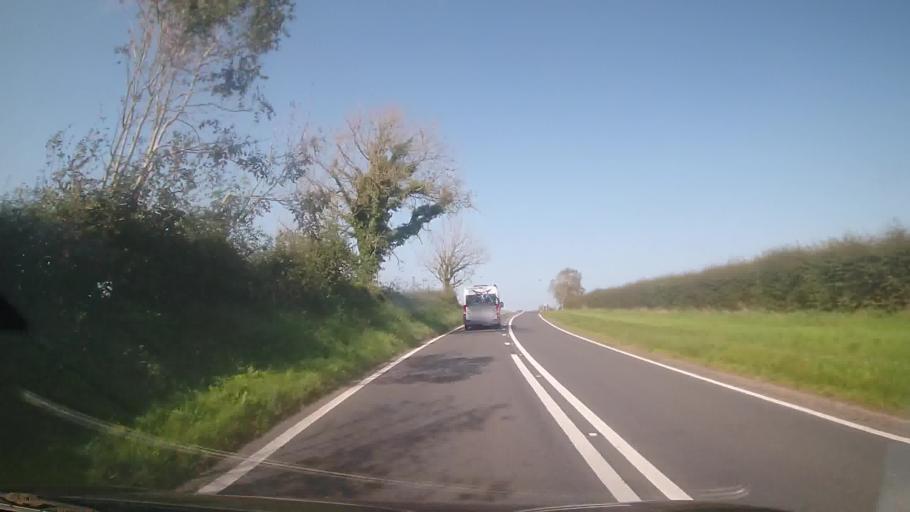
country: GB
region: Wales
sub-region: County of Ceredigion
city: Cardigan
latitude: 52.0382
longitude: -4.6970
